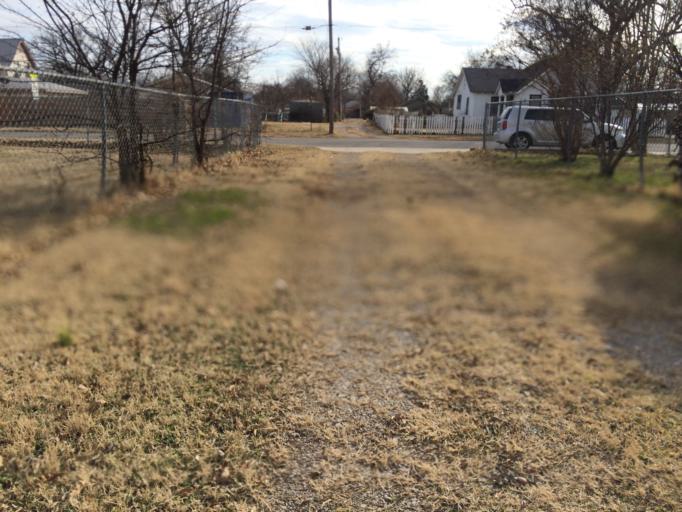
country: US
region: Oklahoma
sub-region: Cleveland County
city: Norman
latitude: 35.2270
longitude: -97.4364
